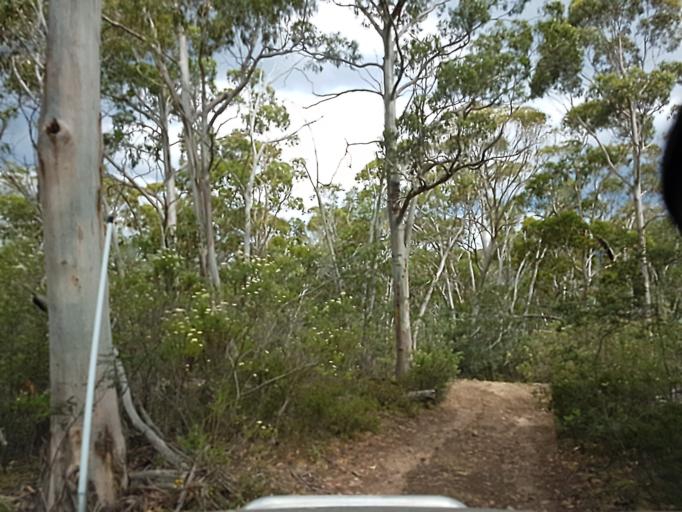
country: AU
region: New South Wales
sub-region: Snowy River
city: Jindabyne
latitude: -36.8787
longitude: 148.2010
